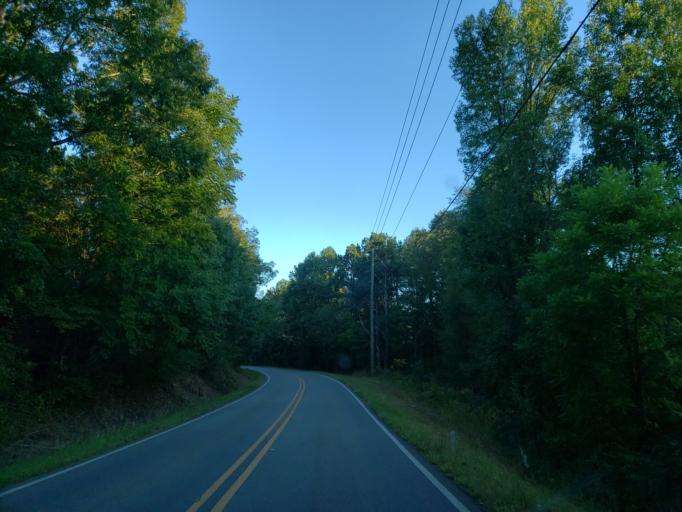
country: US
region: Georgia
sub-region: Bartow County
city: Rydal
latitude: 34.3748
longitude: -84.5890
